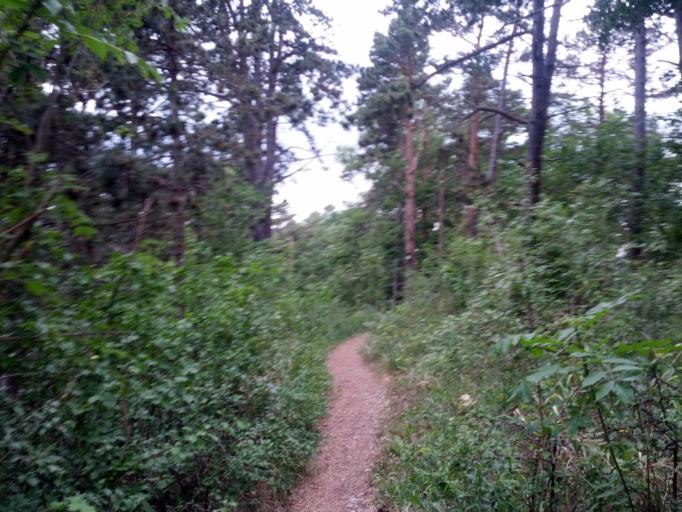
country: DE
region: Thuringia
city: Eisenach
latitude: 50.9879
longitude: 10.2910
